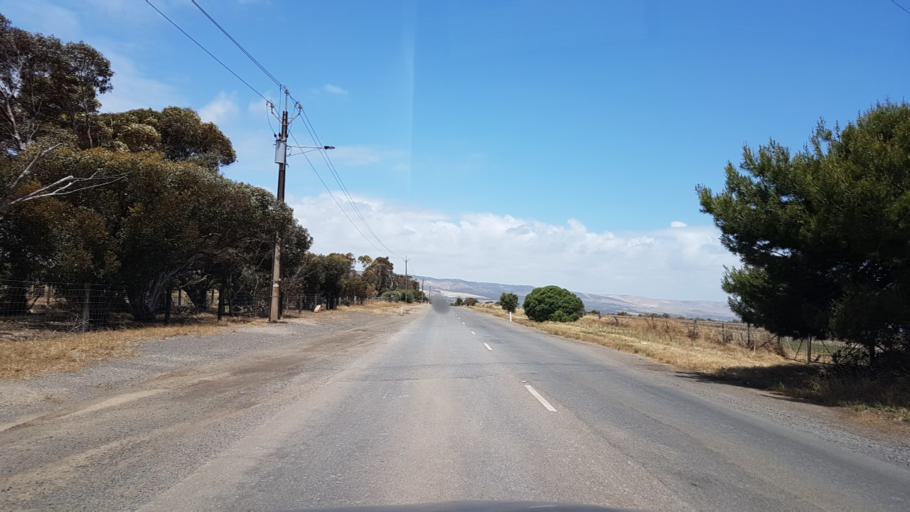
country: AU
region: South Australia
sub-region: Onkaparinga
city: Aldinga
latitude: -35.2567
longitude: 138.4825
